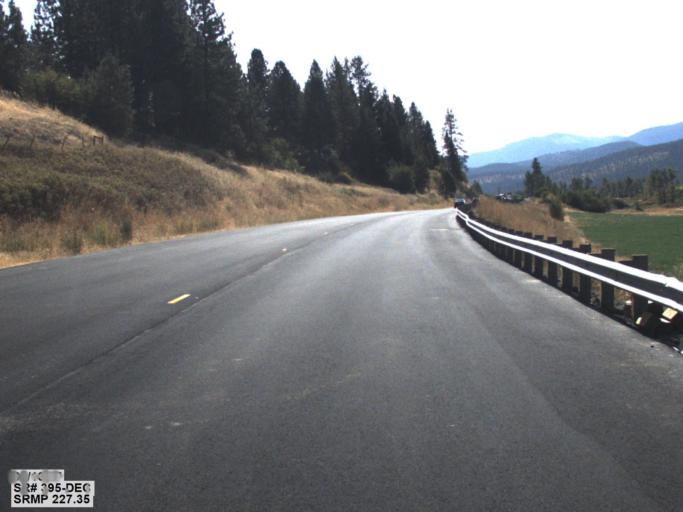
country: US
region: Washington
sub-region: Stevens County
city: Colville
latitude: 48.5140
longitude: -117.9001
